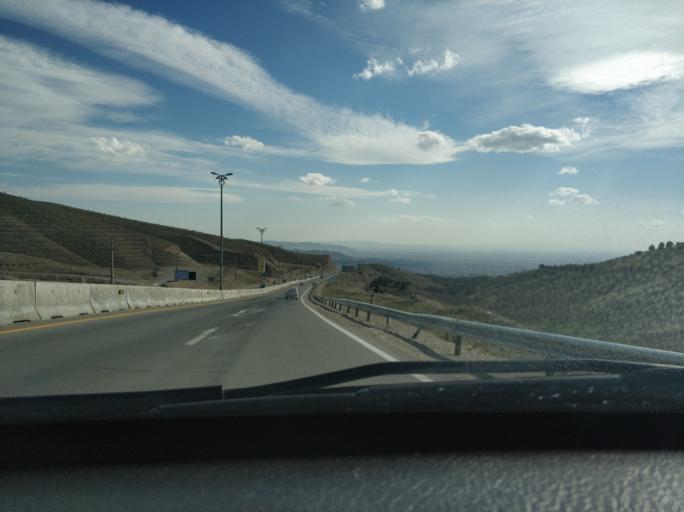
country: IR
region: Tehran
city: Tajrish
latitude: 35.7961
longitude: 51.5711
